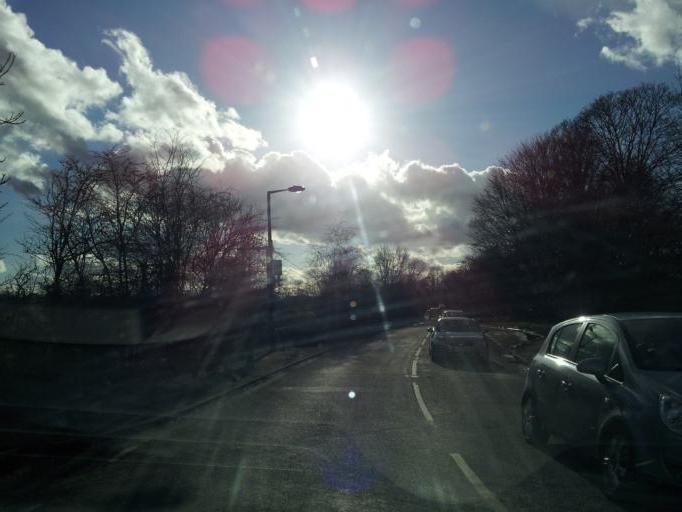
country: GB
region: England
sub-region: Derbyshire
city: Alfreton
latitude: 53.1132
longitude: -1.3732
